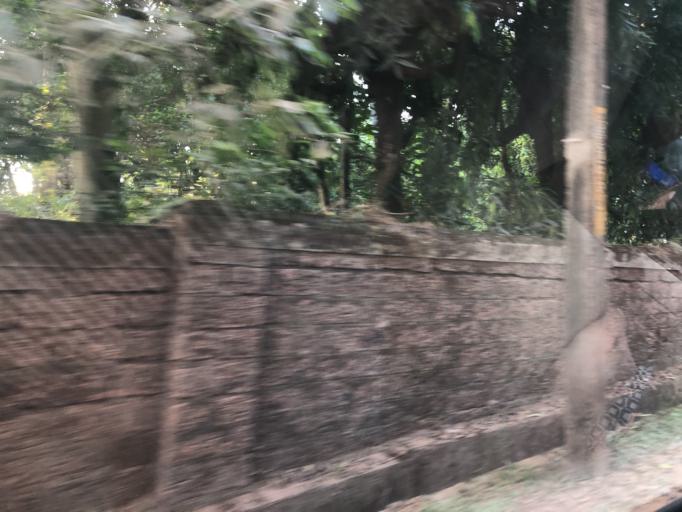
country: IN
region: Karnataka
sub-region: Dakshina Kannada
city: Ullal
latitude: 12.8430
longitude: 74.8473
